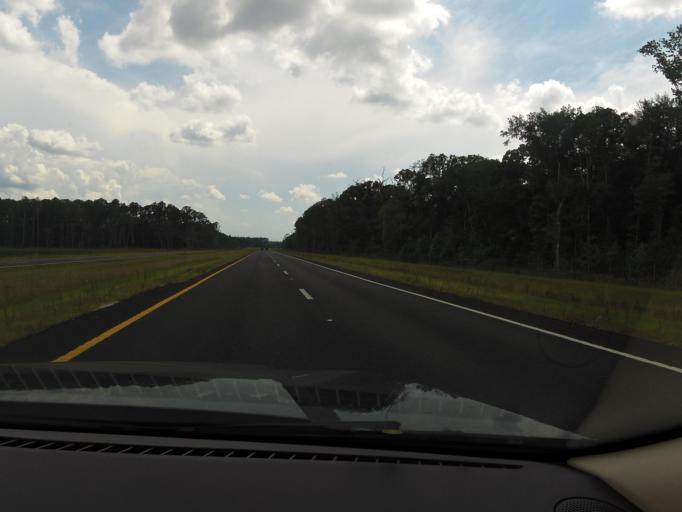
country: US
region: Florida
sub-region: Duval County
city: Baldwin
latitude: 30.3208
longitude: -81.9722
